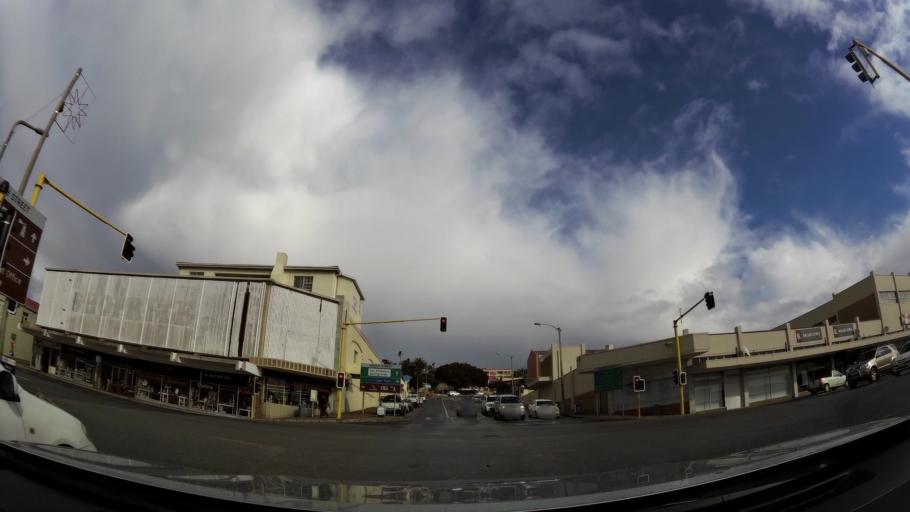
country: ZA
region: Western Cape
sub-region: Eden District Municipality
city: Mossel Bay
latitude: -34.1824
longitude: 22.1428
